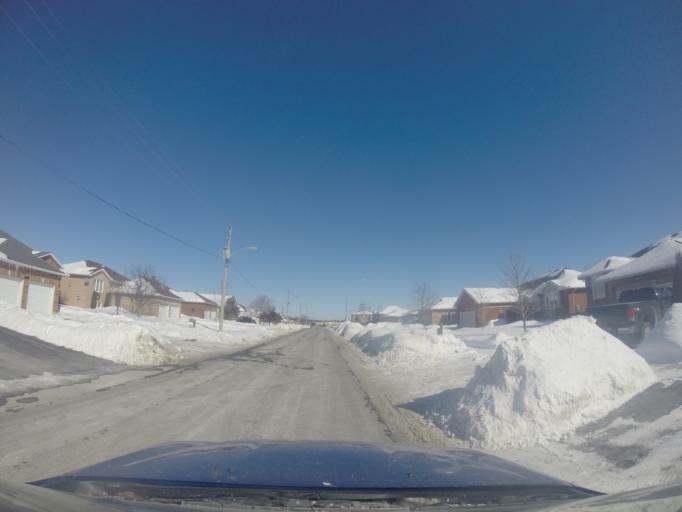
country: CA
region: Ontario
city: Omemee
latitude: 44.3402
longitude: -78.7503
